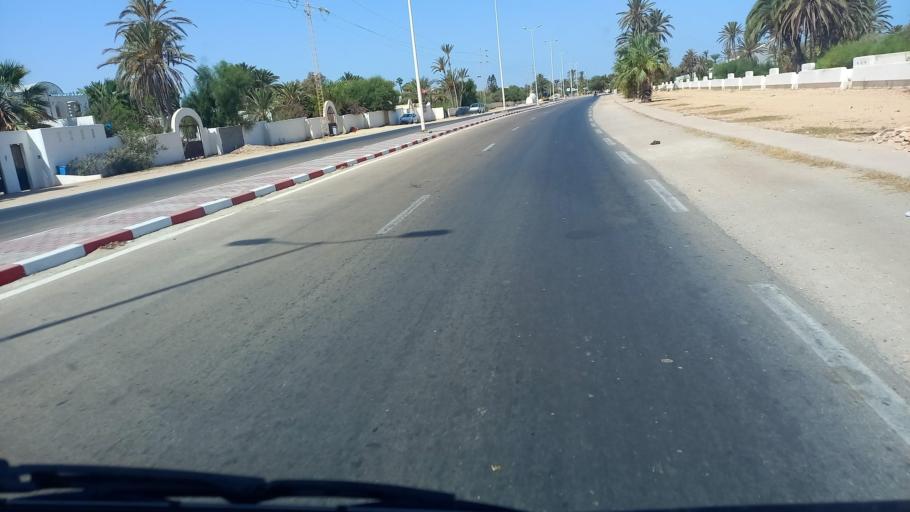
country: TN
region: Madanin
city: Midoun
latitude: 33.8266
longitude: 11.0343
